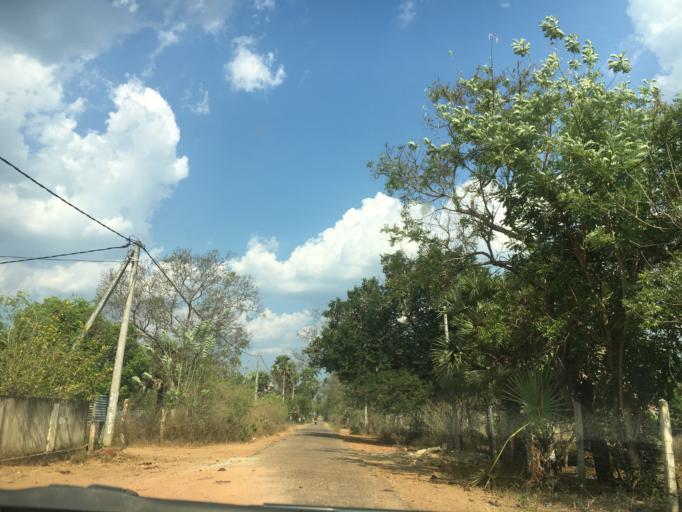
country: LK
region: Northern Province
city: Kilinochchi
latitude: 9.1395
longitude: 80.4484
